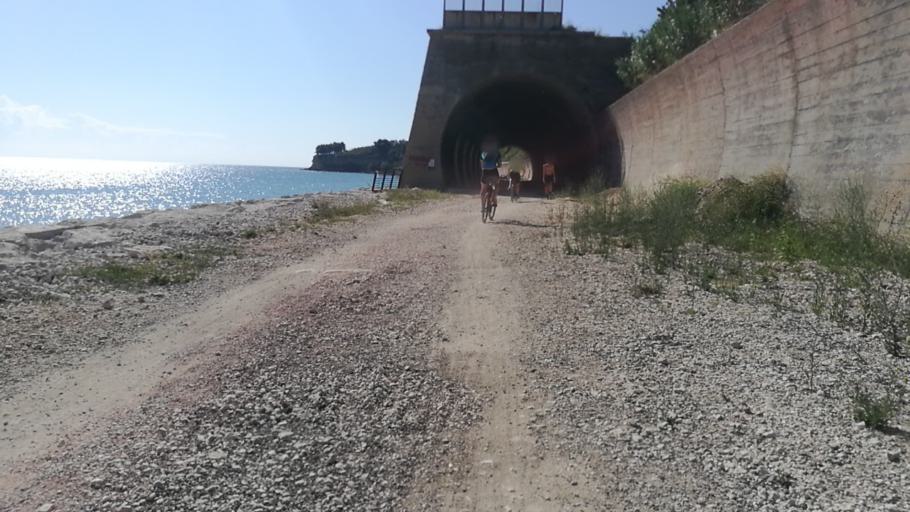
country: IT
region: Abruzzo
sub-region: Provincia di Chieti
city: Ortona
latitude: 42.3409
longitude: 14.4153
